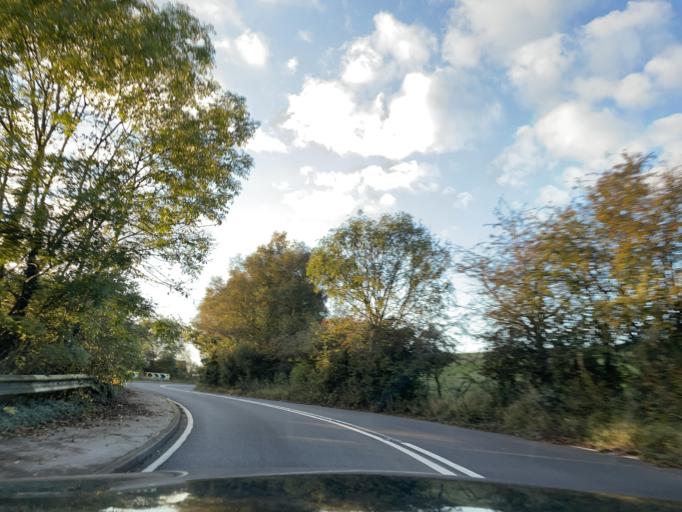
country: GB
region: England
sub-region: Borough of Stockport
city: Marple
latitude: 53.4126
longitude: -2.0334
